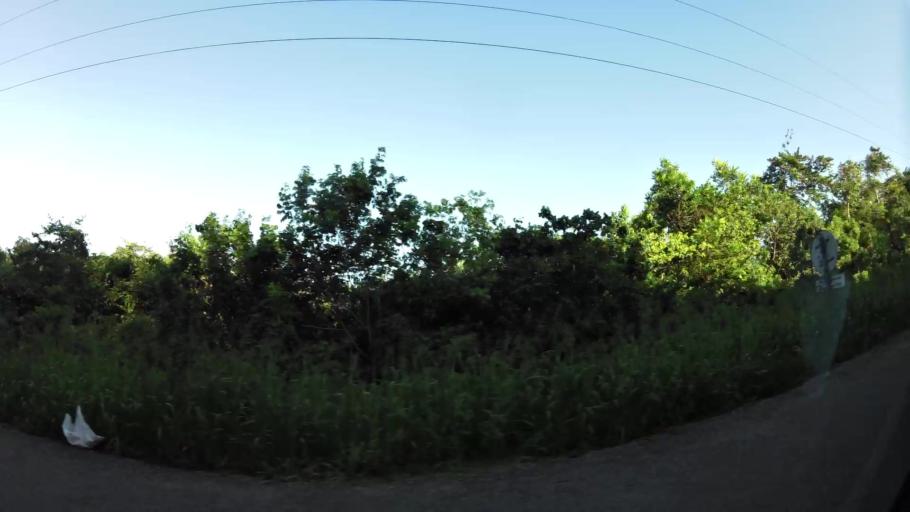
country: GF
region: Guyane
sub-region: Guyane
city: Remire-Montjoly
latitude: 4.8865
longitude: -52.2955
